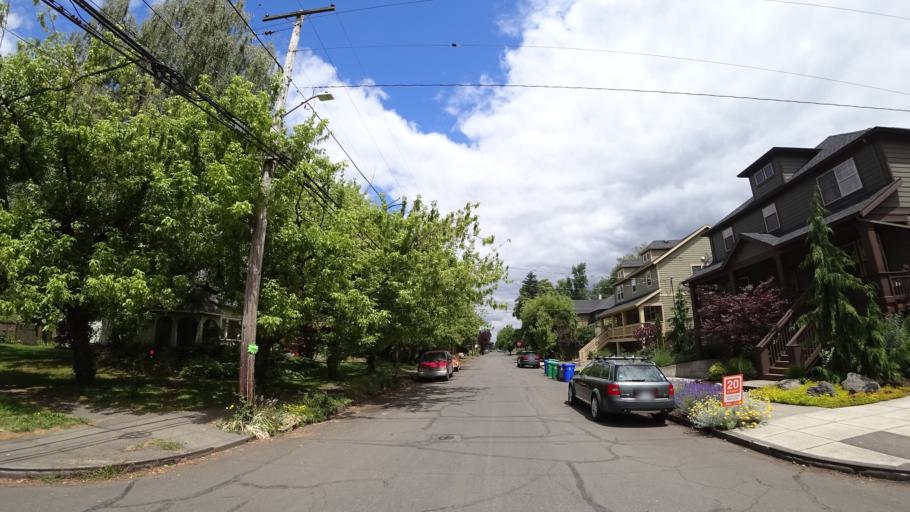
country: US
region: Oregon
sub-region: Multnomah County
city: Portland
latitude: 45.5761
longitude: -122.7215
